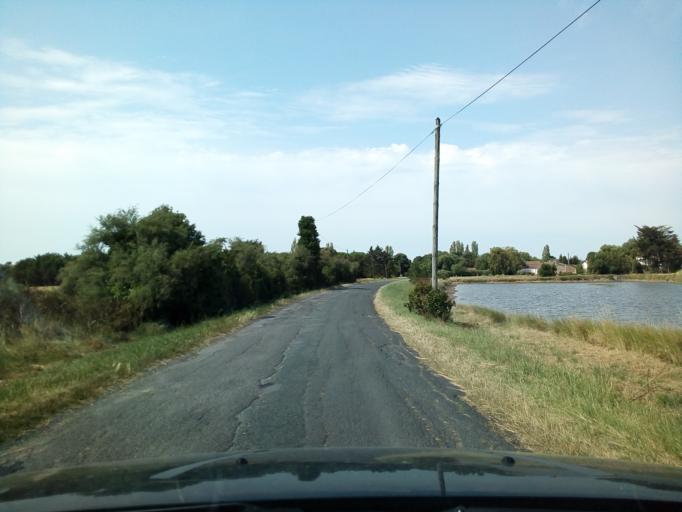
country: FR
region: Poitou-Charentes
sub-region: Departement de la Charente-Maritime
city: Boyard-Ville
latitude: 45.9584
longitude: -1.2558
